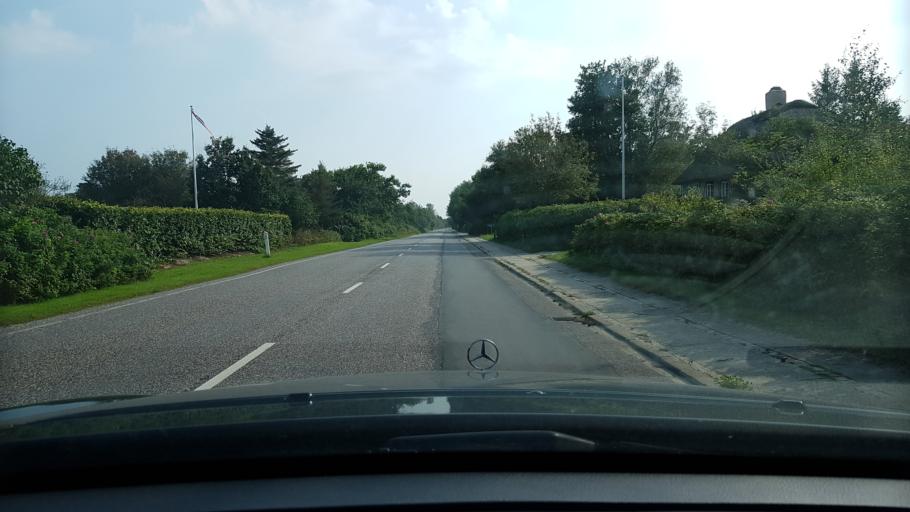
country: DK
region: North Denmark
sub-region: Alborg Kommune
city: Hals
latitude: 56.8162
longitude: 10.2710
